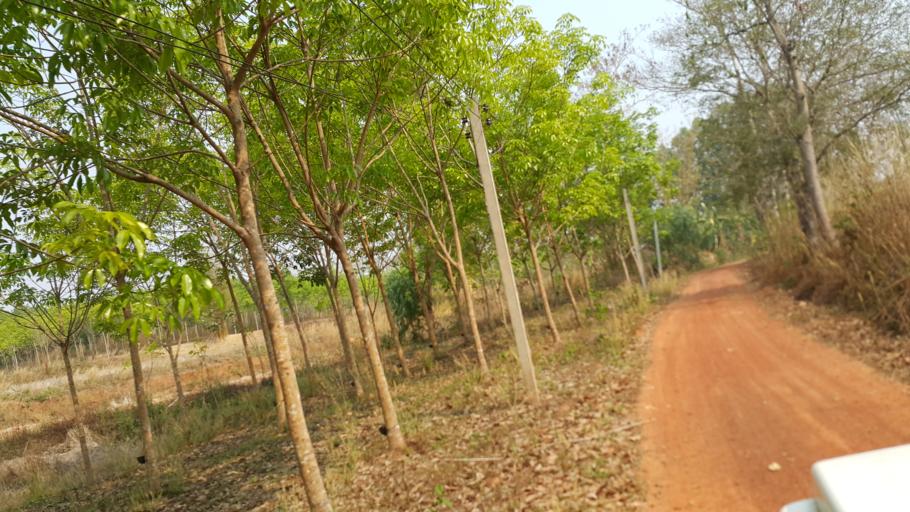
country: TH
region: Nakhon Phanom
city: Ban Phaeng
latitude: 17.8268
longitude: 104.2471
